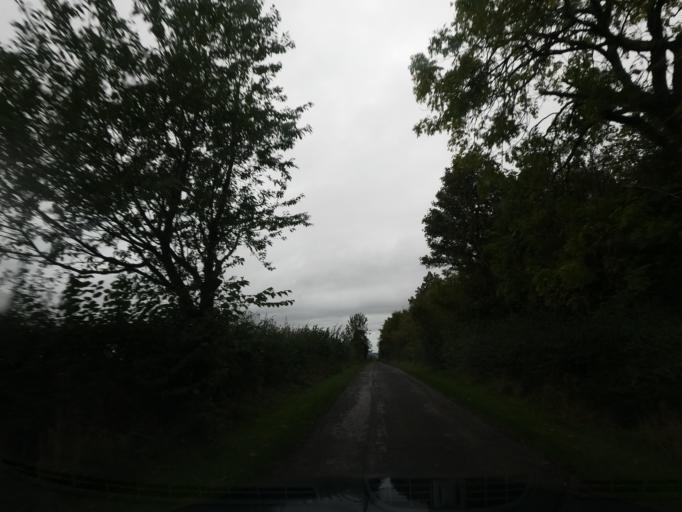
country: GB
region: England
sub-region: Northumberland
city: Ford
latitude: 55.6962
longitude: -2.0860
